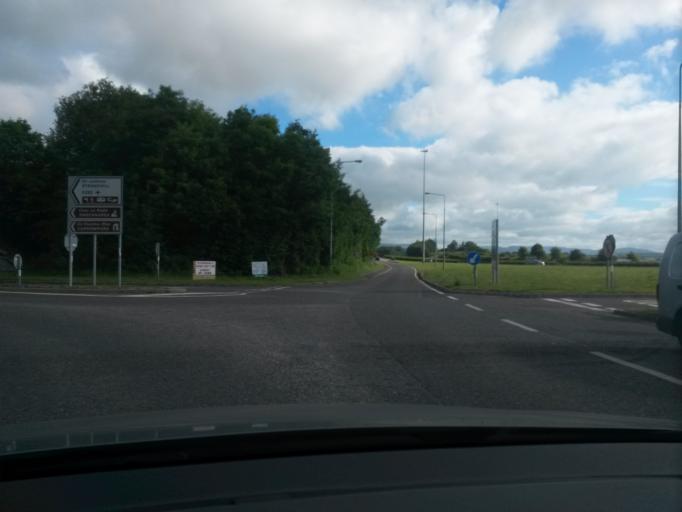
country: IE
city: Ballisodare
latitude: 54.2214
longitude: -8.5013
